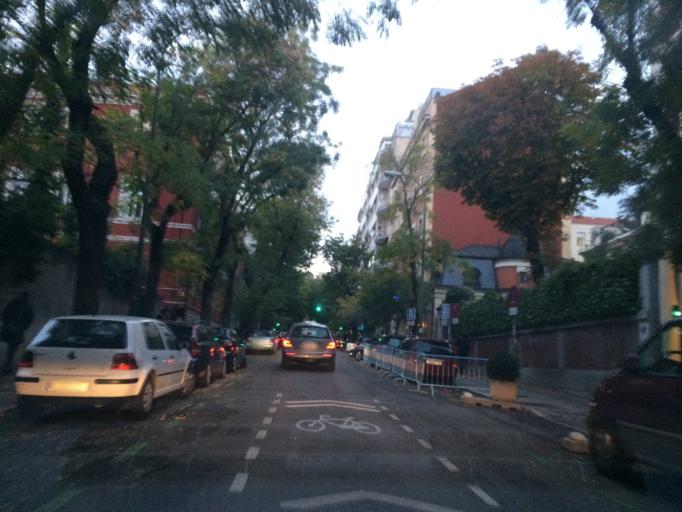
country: ES
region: Madrid
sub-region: Provincia de Madrid
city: Salamanca
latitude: 40.4281
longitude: -3.6924
